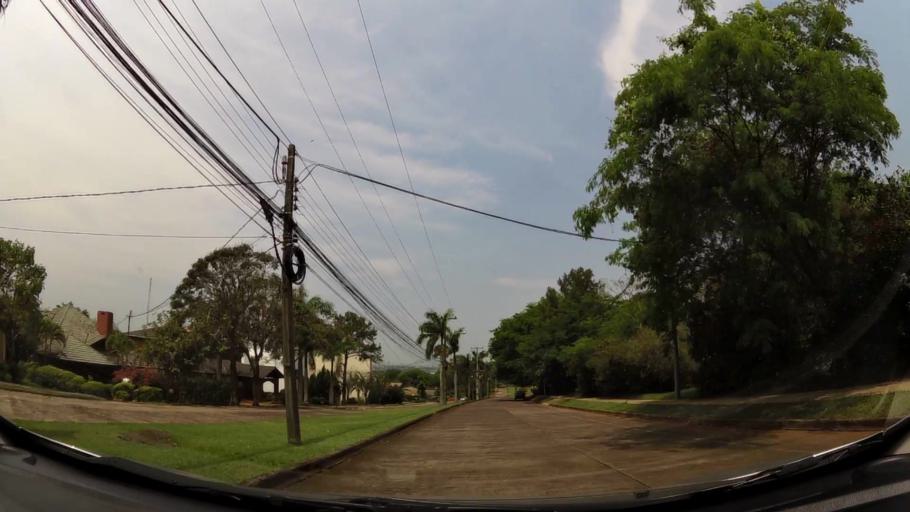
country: PY
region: Alto Parana
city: Ciudad del Este
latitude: -25.4929
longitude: -54.6119
